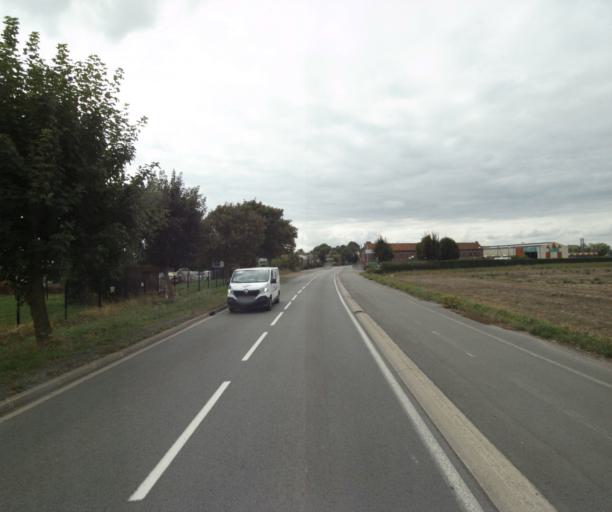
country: FR
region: Nord-Pas-de-Calais
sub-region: Departement du Nord
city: Anstaing
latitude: 50.6101
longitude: 3.1839
